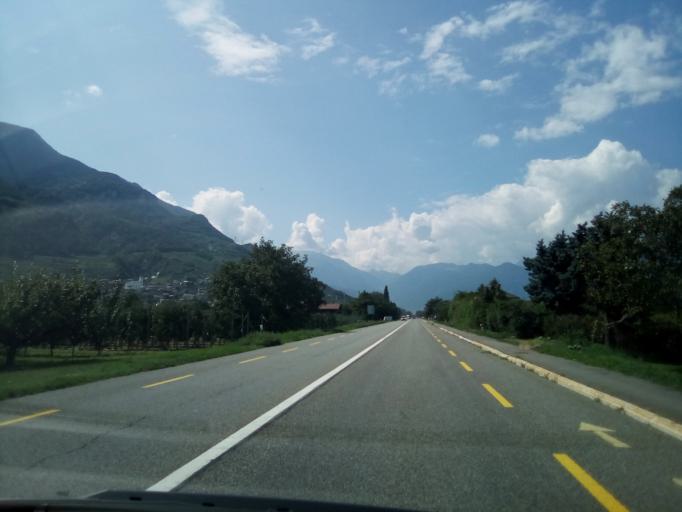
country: CH
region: Valais
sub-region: Martigny District
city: Saxon
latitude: 46.1560
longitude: 7.1885
